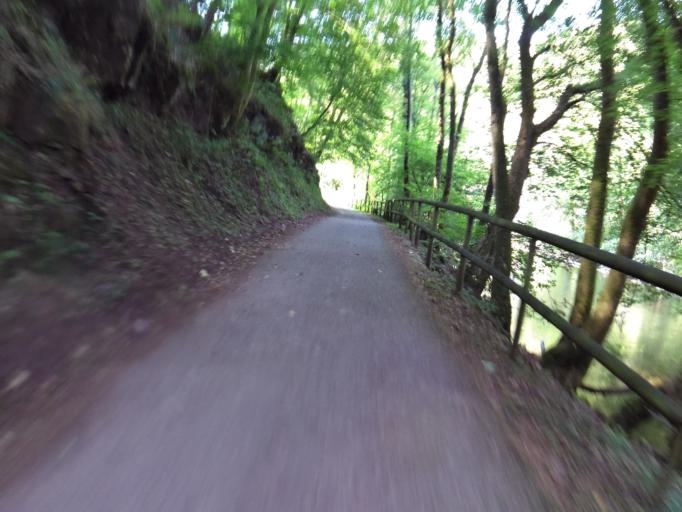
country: DE
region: Rheinland-Pfalz
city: Dahlem
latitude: 49.9148
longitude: 6.6116
